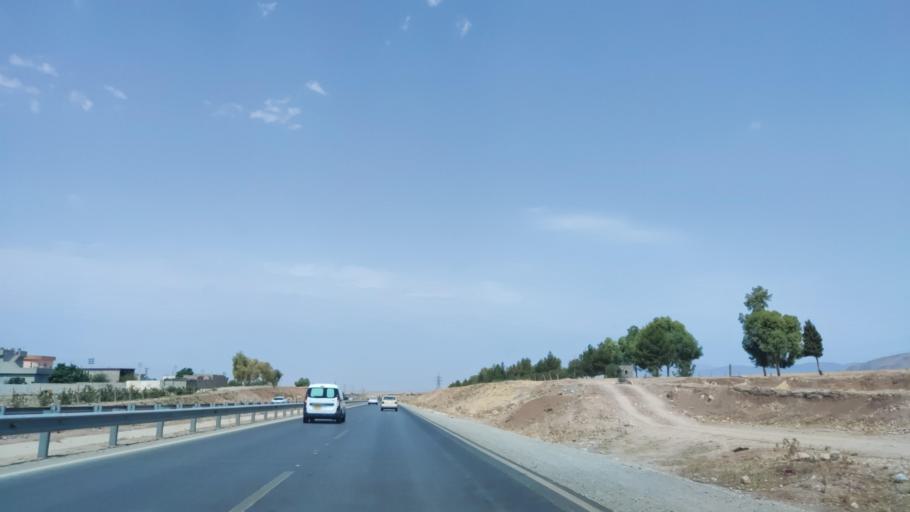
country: IQ
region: Arbil
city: Shaqlawah
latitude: 36.4997
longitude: 44.3600
